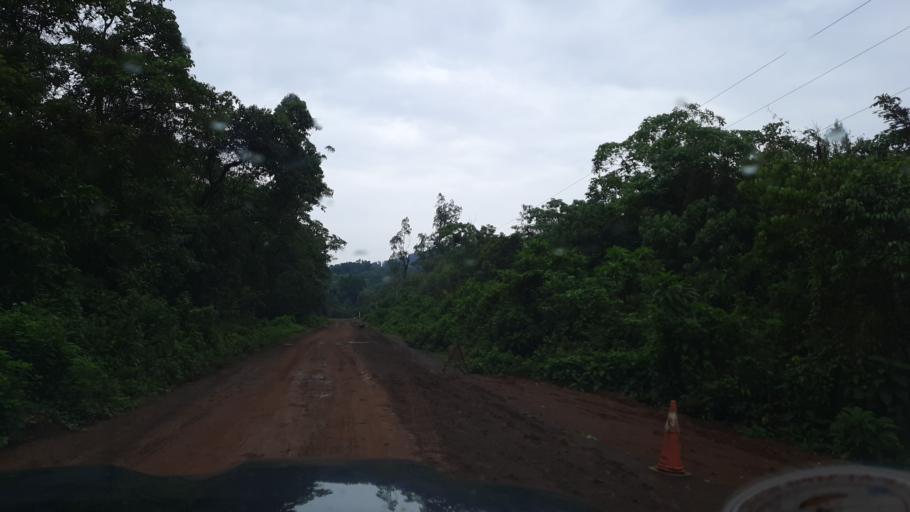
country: ET
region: Oromiya
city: Gore
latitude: 7.8699
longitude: 35.4801
